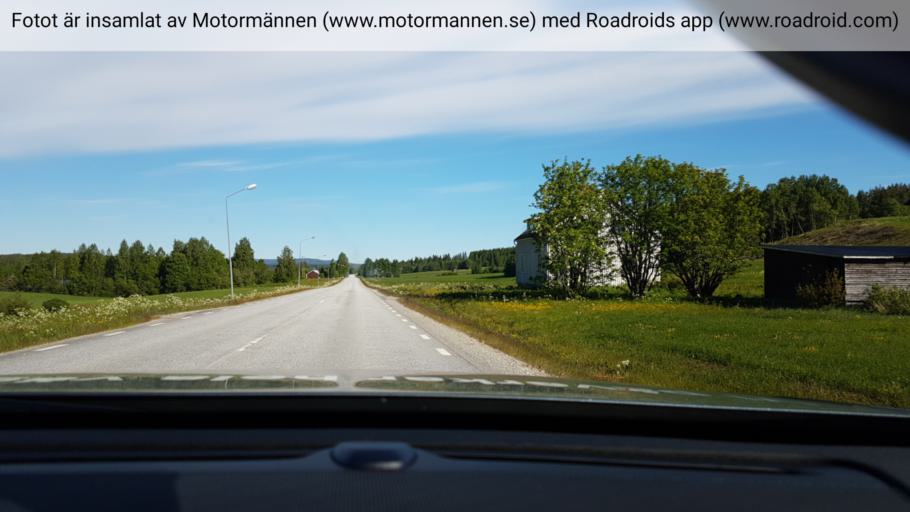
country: SE
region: Vaesterbotten
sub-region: Vindelns Kommun
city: Vindeln
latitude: 64.1695
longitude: 19.4911
